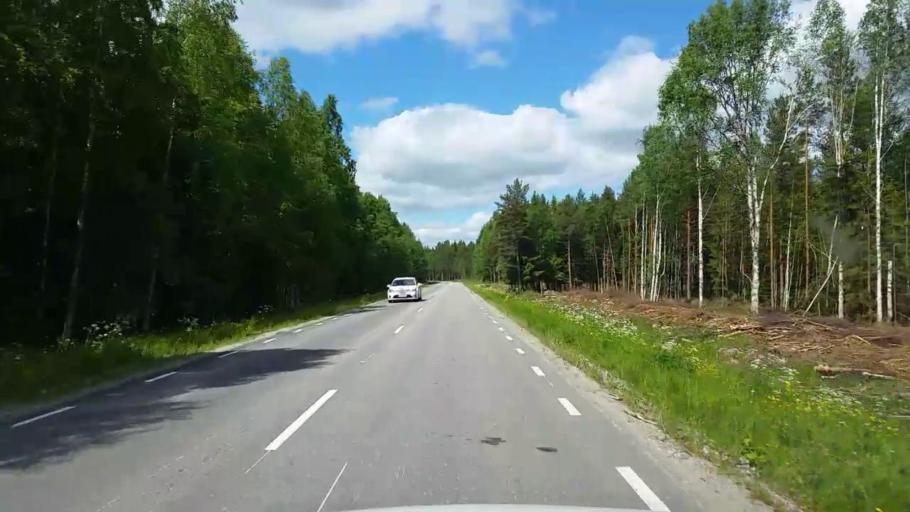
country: SE
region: Gaevleborg
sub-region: Ovanakers Kommun
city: Alfta
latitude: 61.2699
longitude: 16.1171
